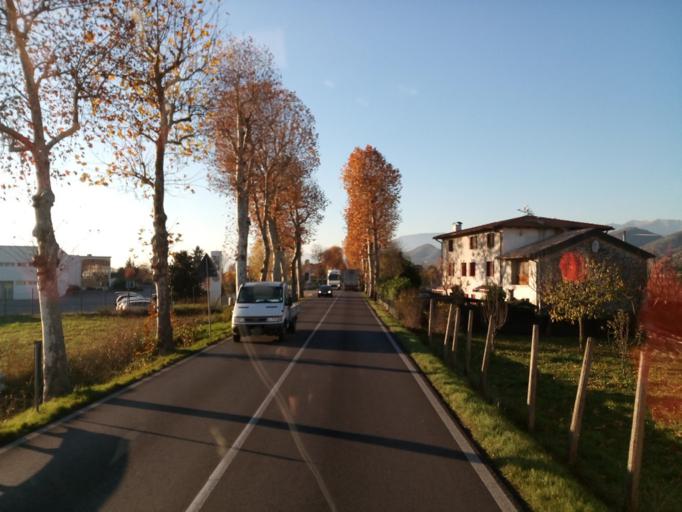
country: IT
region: Veneto
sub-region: Provincia di Treviso
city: Maser
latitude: 45.7918
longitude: 11.9783
